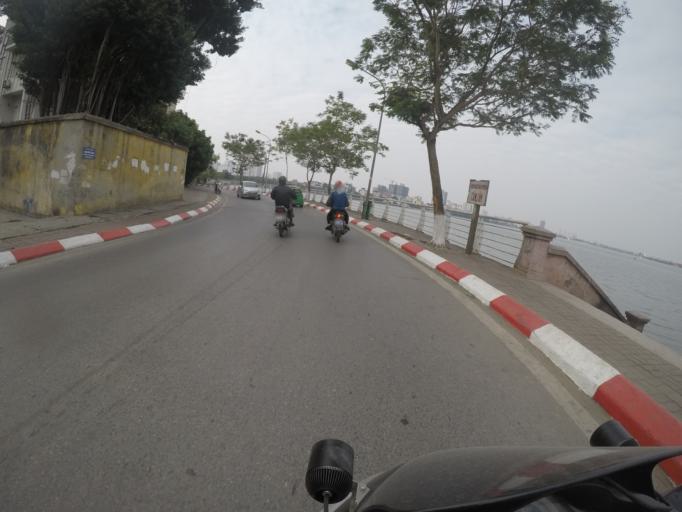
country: VN
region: Ha Noi
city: Tay Ho
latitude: 21.0553
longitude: 105.8116
